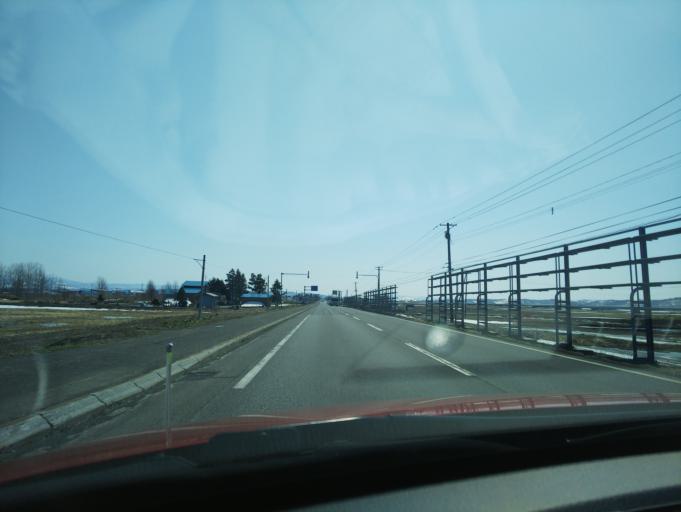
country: JP
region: Hokkaido
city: Nayoro
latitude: 44.2191
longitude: 142.3949
